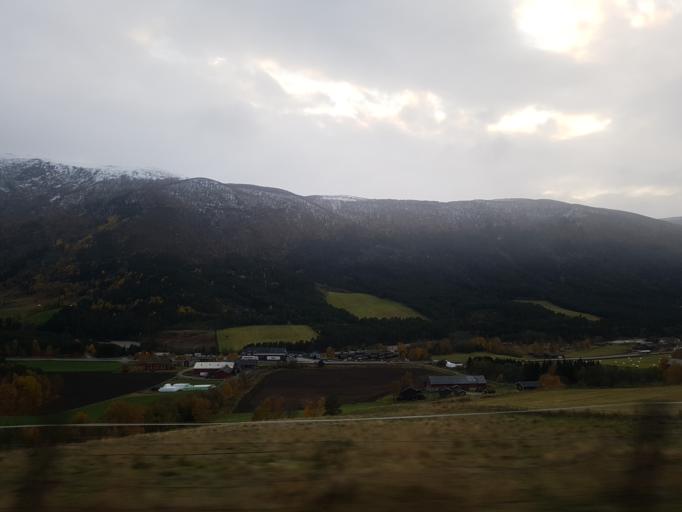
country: NO
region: Oppland
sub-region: Dovre
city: Dovre
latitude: 62.0172
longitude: 9.1979
